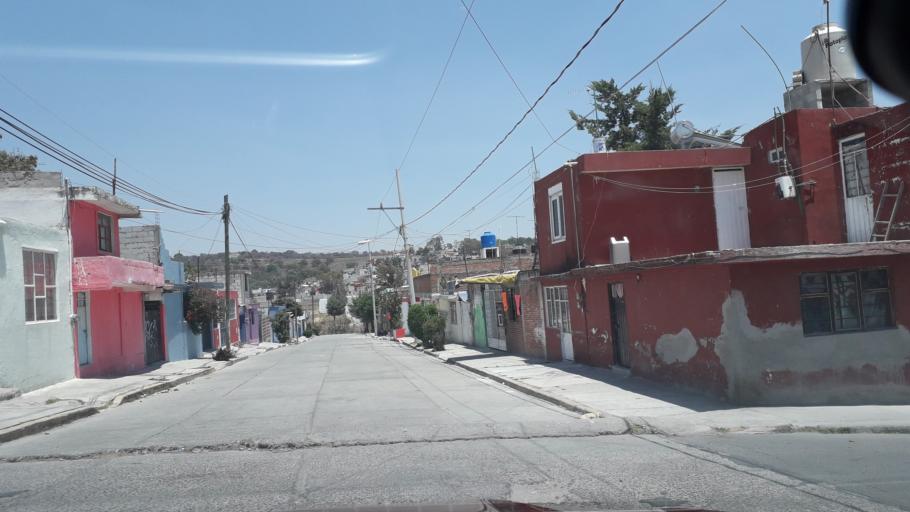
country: MX
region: Puebla
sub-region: Puebla
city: Galaxia la Calera
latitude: 18.9939
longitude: -98.1760
